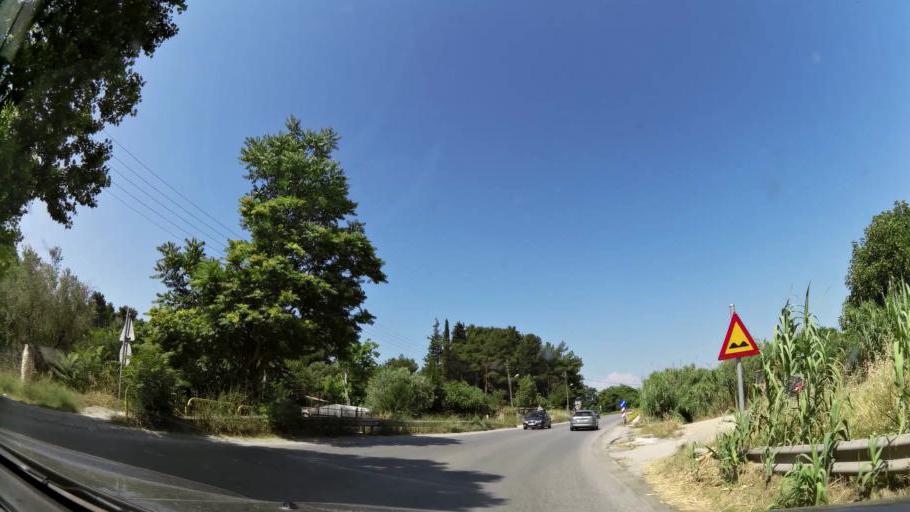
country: GR
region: Central Macedonia
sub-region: Nomos Thessalonikis
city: Neoi Epivates
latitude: 40.5001
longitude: 22.9085
